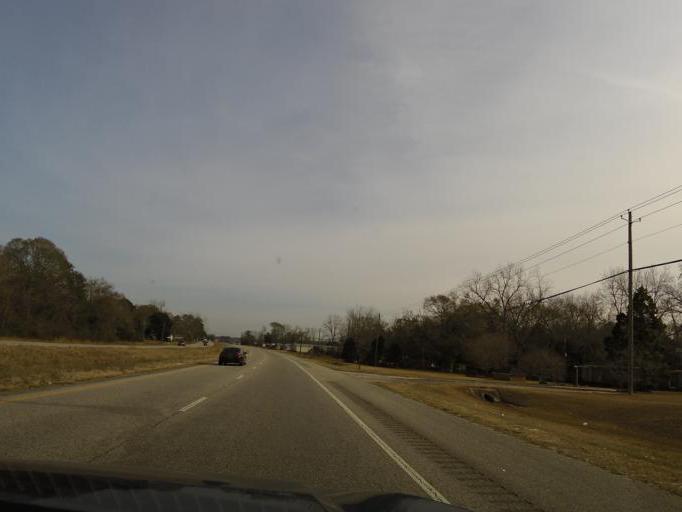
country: US
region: Alabama
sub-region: Houston County
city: Cowarts
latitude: 31.1930
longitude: -85.3154
